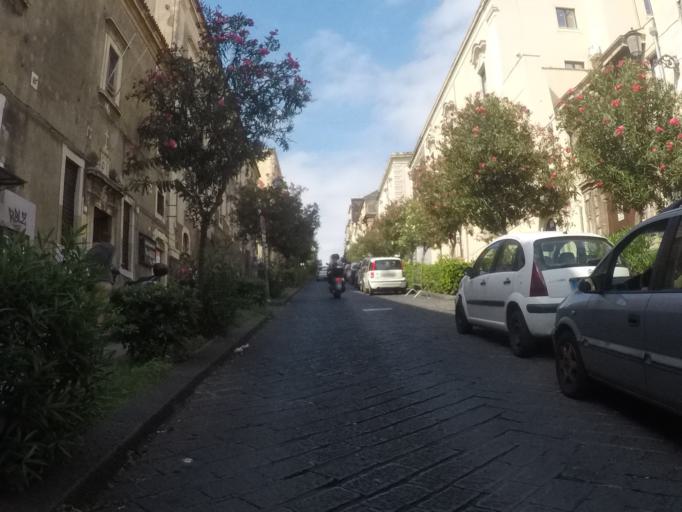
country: IT
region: Sicily
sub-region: Catania
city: Catania
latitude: 37.5050
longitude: 15.0856
